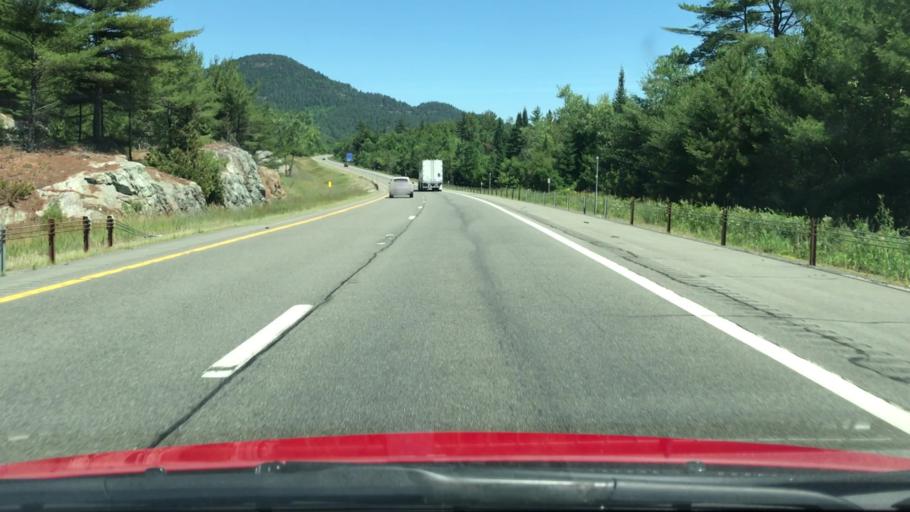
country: US
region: New York
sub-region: Essex County
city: Mineville
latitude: 43.9805
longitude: -73.7234
